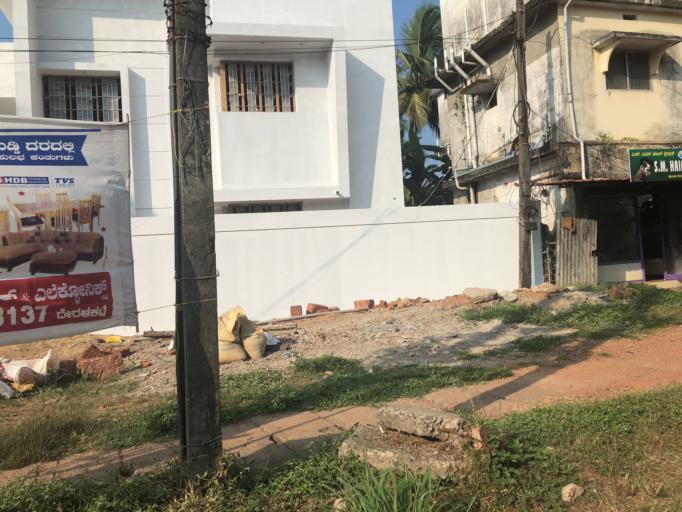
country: IN
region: Karnataka
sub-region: Dakshina Kannada
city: Ullal
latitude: 12.8210
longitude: 74.8422
